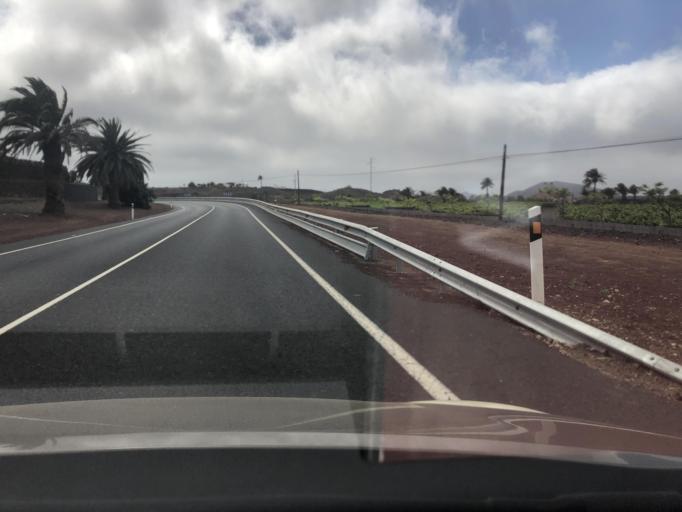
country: ES
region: Canary Islands
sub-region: Provincia de Las Palmas
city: Yaiza
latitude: 28.9503
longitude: -13.7510
